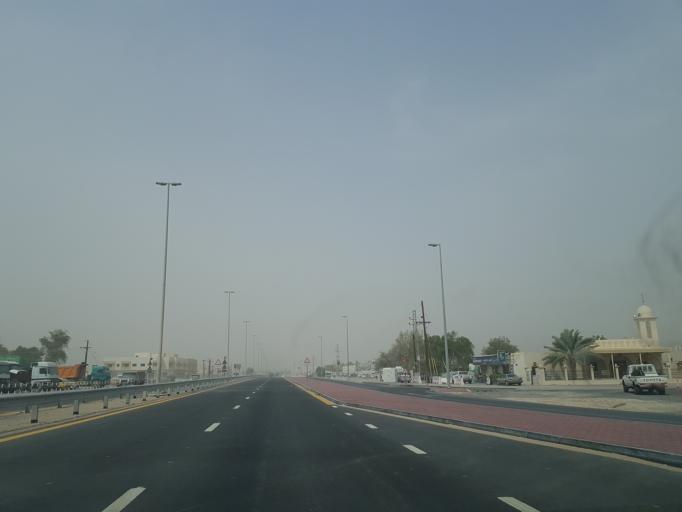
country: AE
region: Dubai
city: Dubai
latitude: 24.9527
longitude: 55.4982
